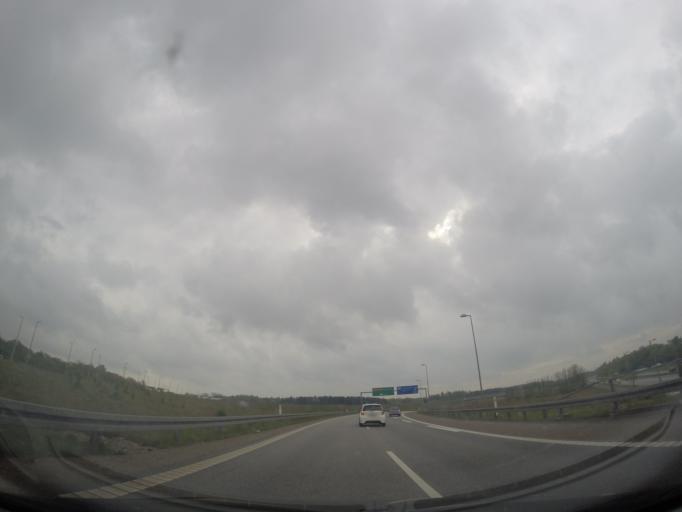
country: DK
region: Capital Region
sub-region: Rodovre Kommune
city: Rodovre
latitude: 55.6917
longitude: 12.4342
